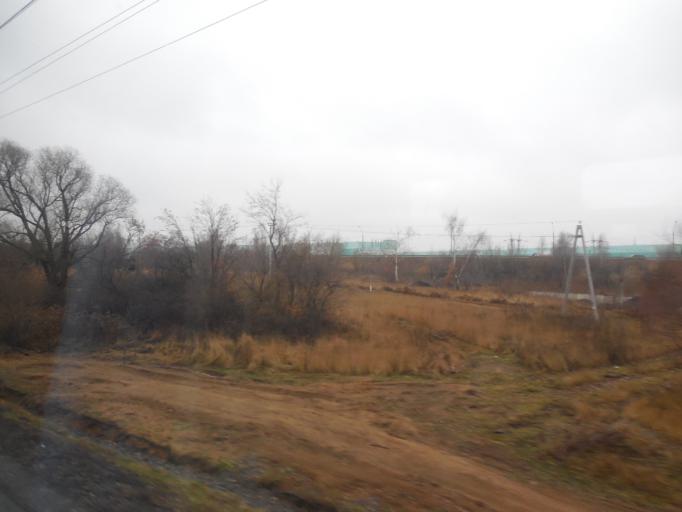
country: RU
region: Moskovskaya
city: Yam
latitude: 55.4791
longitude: 37.7422
